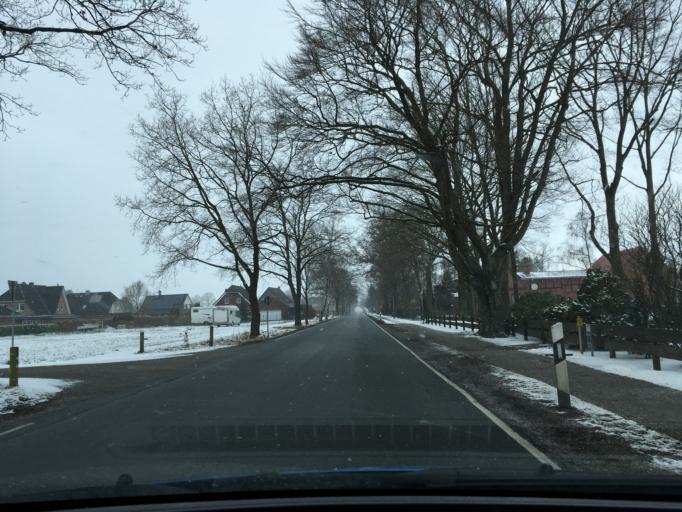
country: DE
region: Lower Saxony
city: Vierhofen
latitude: 53.2721
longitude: 10.2138
